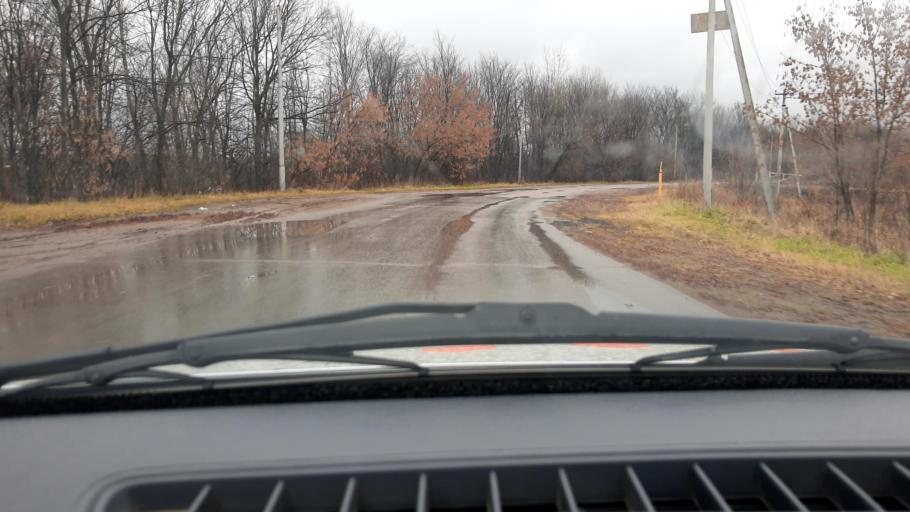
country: RU
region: Bashkortostan
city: Iglino
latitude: 54.7981
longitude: 56.2108
